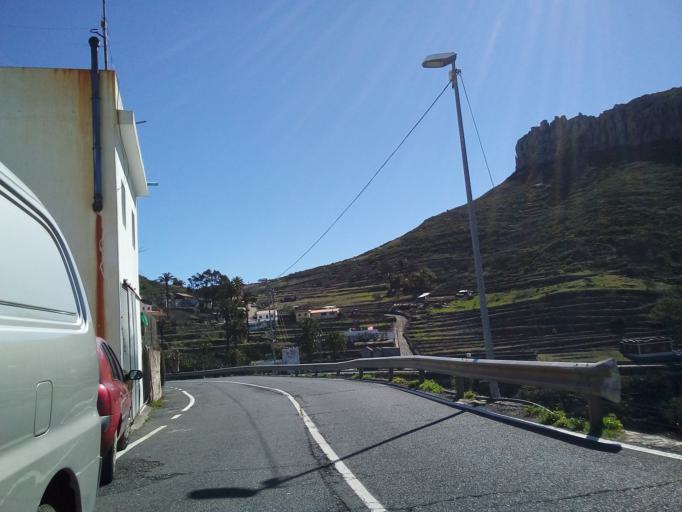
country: ES
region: Canary Islands
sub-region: Provincia de Santa Cruz de Tenerife
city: Alajero
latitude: 28.1054
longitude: -17.2760
